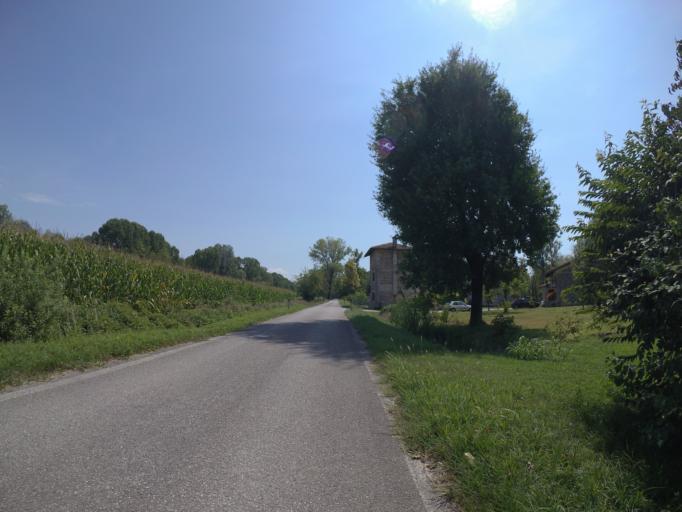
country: IT
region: Friuli Venezia Giulia
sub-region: Provincia di Udine
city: Codroipo
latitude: 45.9404
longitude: 12.9932
